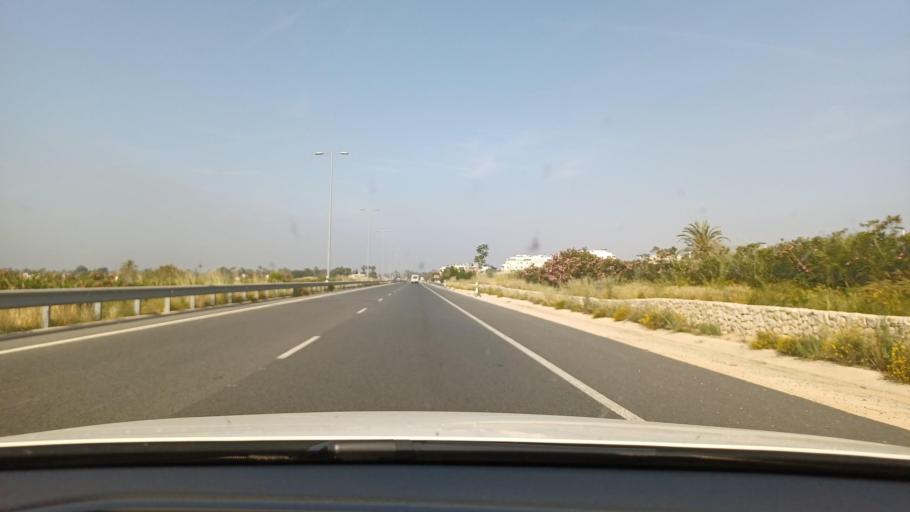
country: ES
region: Valencia
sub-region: Provincia de Alicante
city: Elche
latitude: 38.2616
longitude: -0.6628
